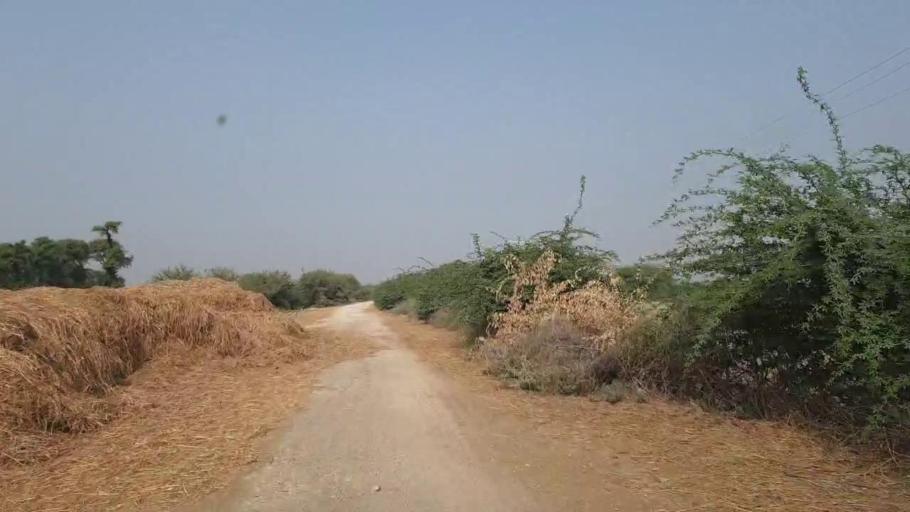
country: PK
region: Sindh
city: Kario
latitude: 24.9292
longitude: 68.6010
